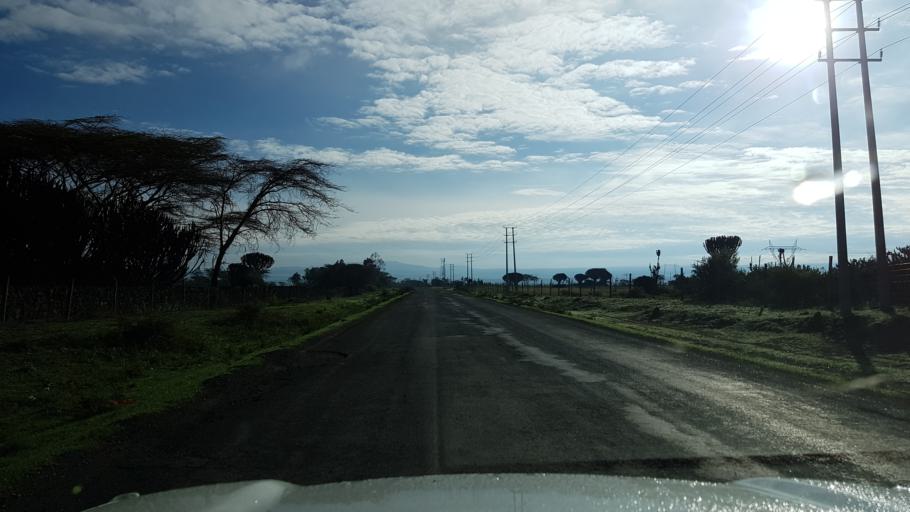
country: KE
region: Nakuru
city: Naivasha
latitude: -0.8188
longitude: 36.3901
